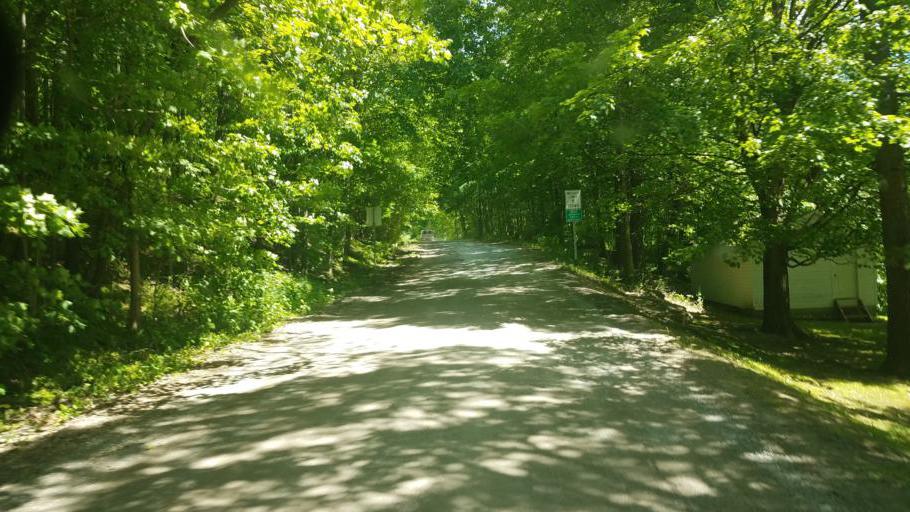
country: US
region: Ohio
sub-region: Geauga County
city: Middlefield
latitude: 41.4205
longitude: -81.0031
